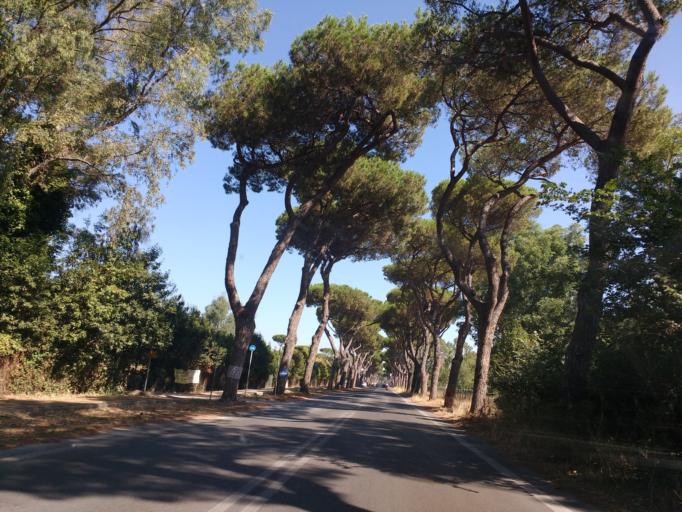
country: IT
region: Latium
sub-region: Citta metropolitana di Roma Capitale
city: Acilia-Castel Fusano-Ostia Antica
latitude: 41.7507
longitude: 12.3095
